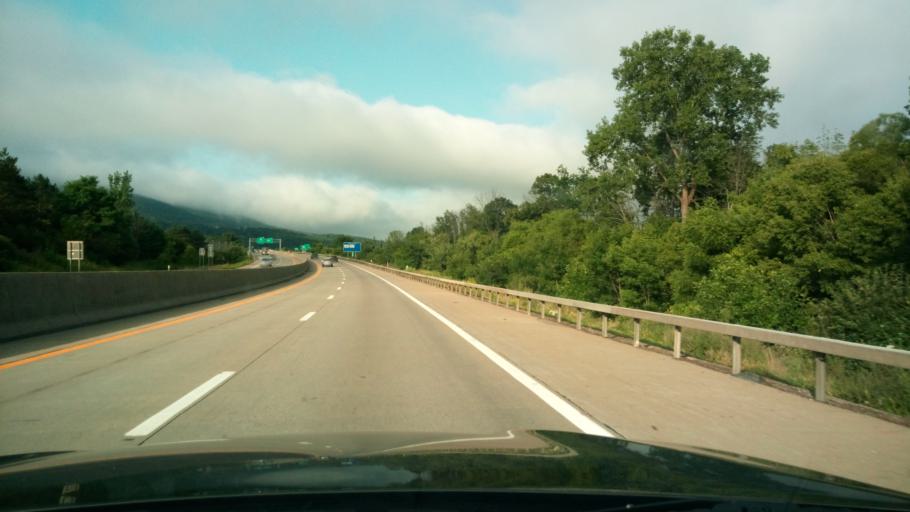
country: US
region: New York
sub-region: Steuben County
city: Painted Post
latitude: 42.1614
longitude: -77.0727
